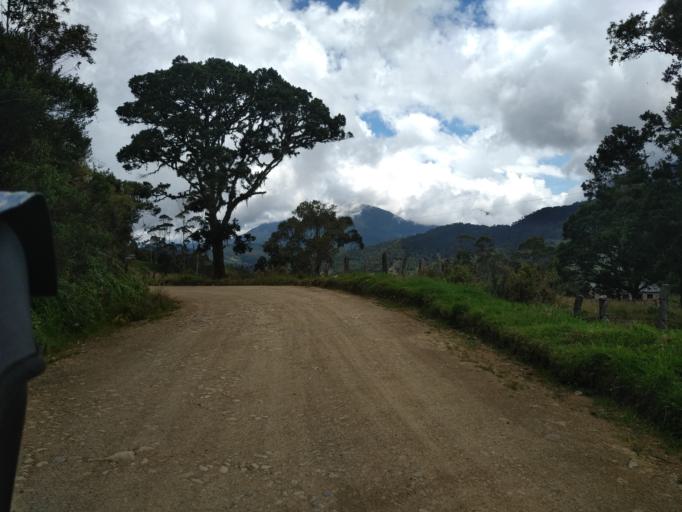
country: CO
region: Boyaca
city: Duitama
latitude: 5.9400
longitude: -73.1220
